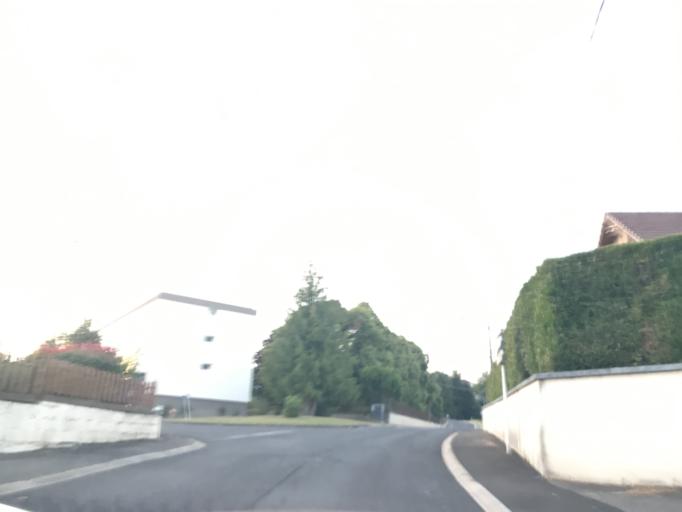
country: FR
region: Auvergne
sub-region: Departement du Puy-de-Dome
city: Saint-Remy-sur-Durolle
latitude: 45.8832
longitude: 3.5922
